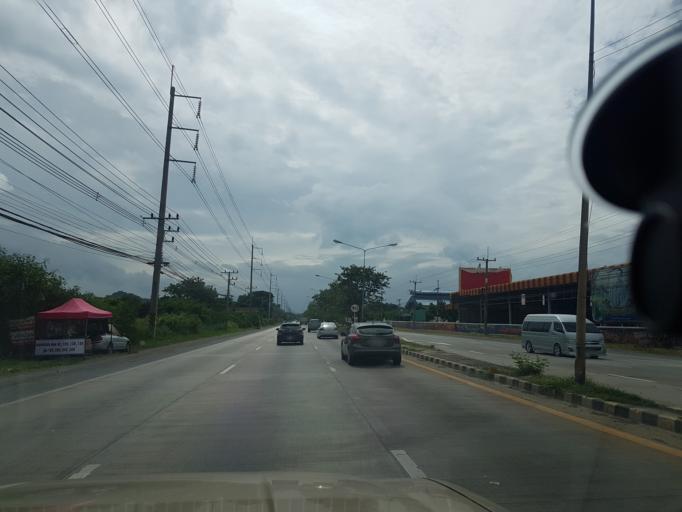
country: TH
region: Sara Buri
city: Phra Phutthabat
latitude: 14.7129
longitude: 100.8250
